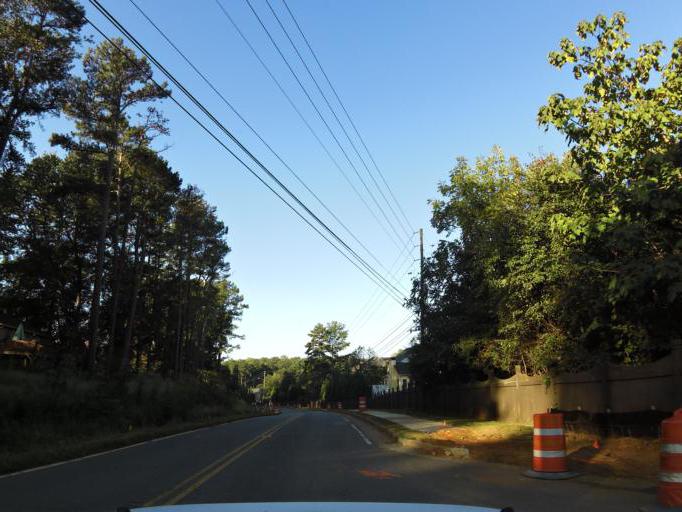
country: US
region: Georgia
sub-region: Cobb County
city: Kennesaw
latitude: 34.0055
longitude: -84.6370
